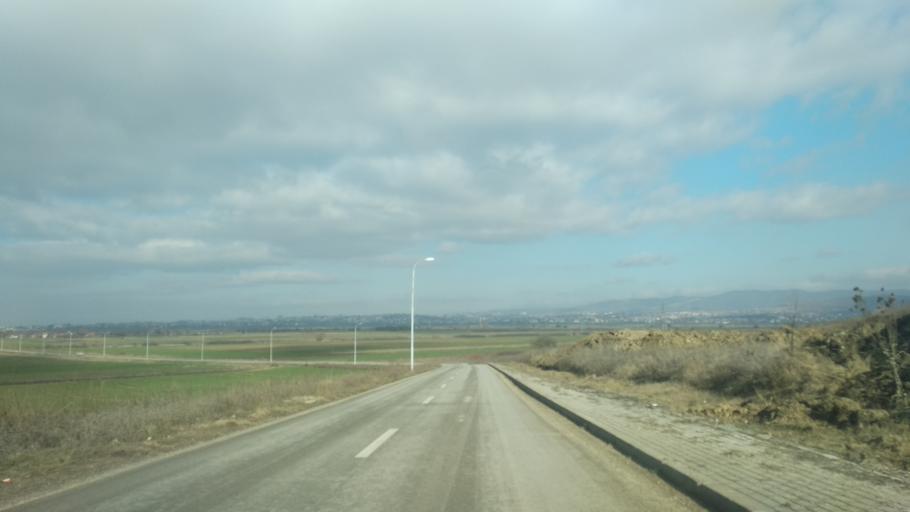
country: XK
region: Pristina
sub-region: Lipjan
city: Lipljan
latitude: 42.5834
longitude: 21.1536
